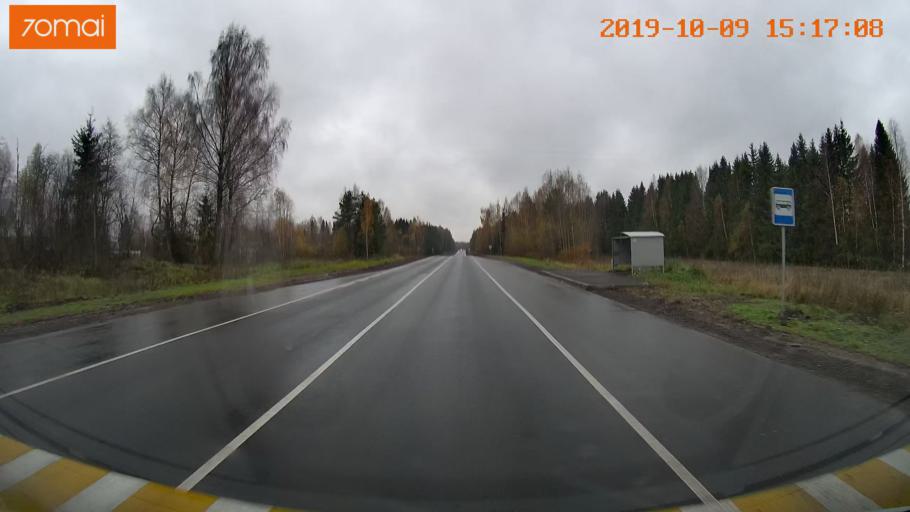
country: RU
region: Kostroma
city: Susanino
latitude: 58.1023
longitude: 41.5838
